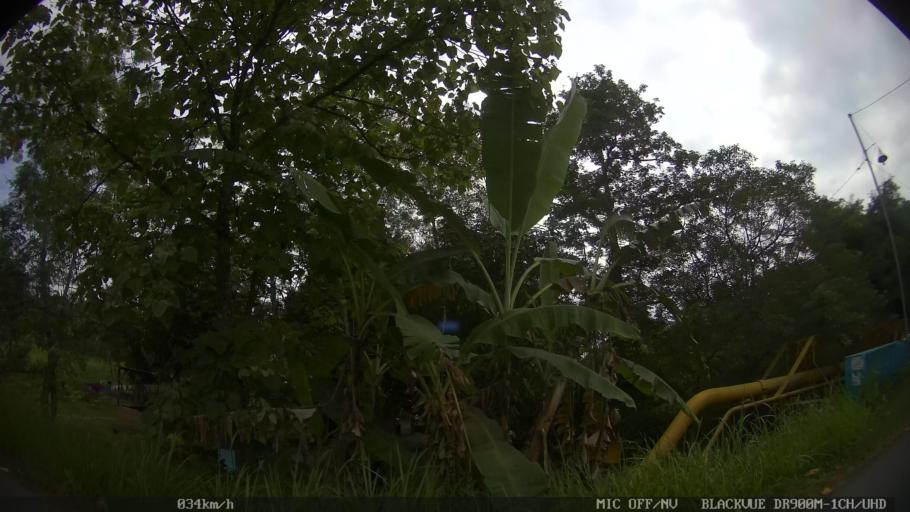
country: ID
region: North Sumatra
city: Sunggal
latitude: 3.6622
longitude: 98.5921
